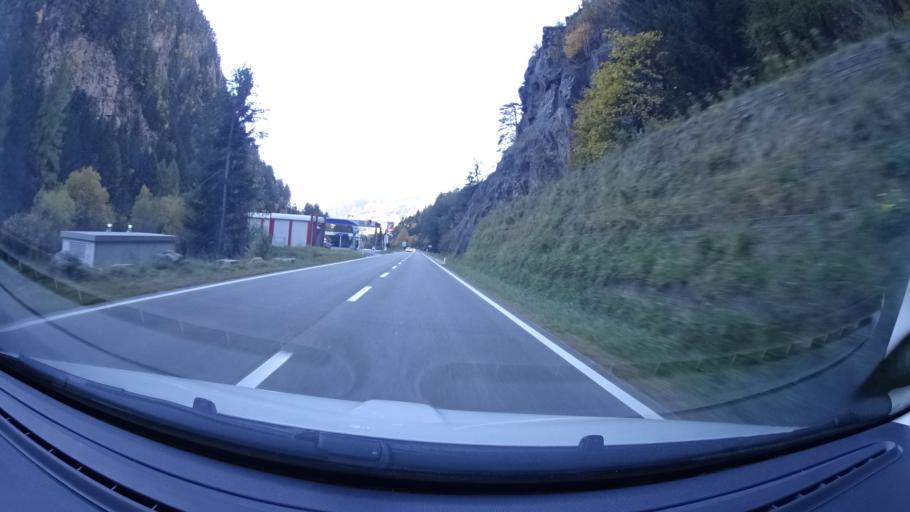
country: IT
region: Trentino-Alto Adige
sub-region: Bolzano
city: Ortisei
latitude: 46.5795
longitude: 11.6405
